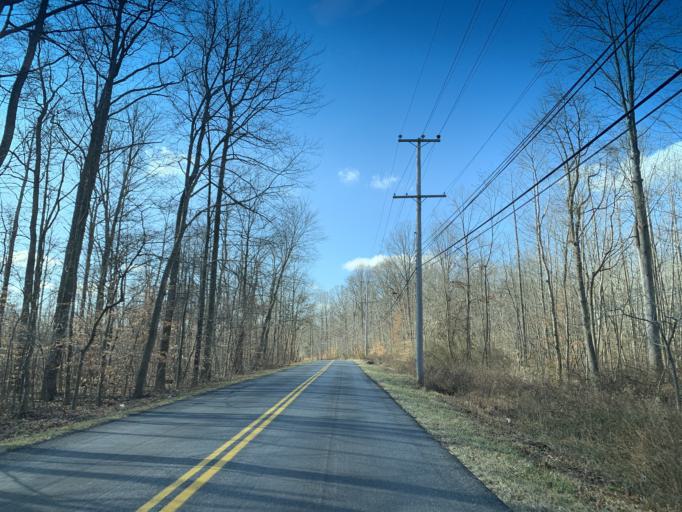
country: US
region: Maryland
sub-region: Harford County
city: Riverside
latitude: 39.5289
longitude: -76.2212
